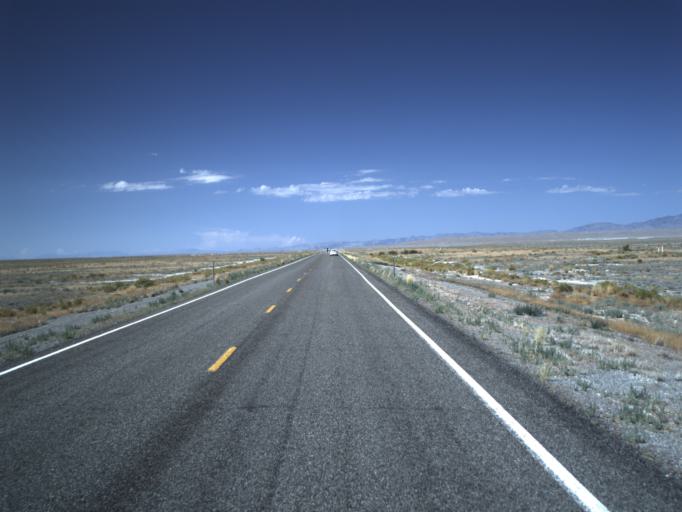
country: US
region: Utah
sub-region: Millard County
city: Delta
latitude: 39.2443
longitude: -112.9079
